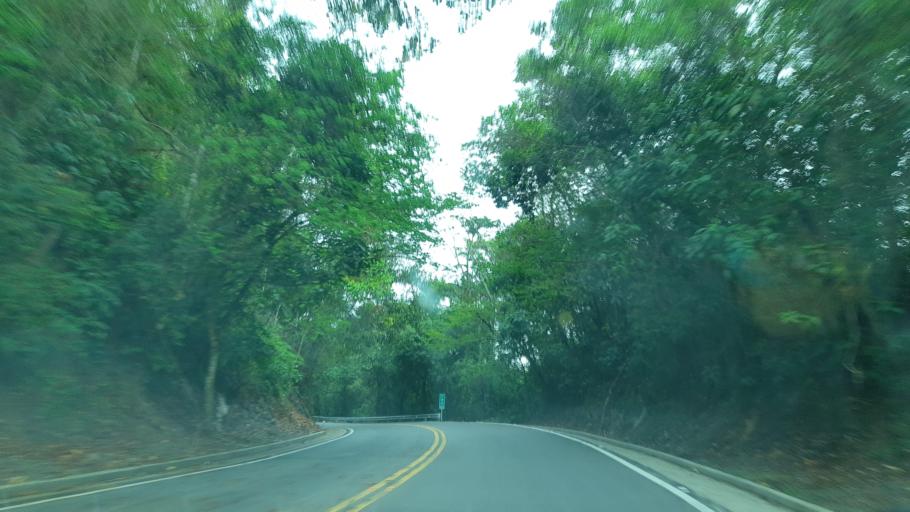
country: CO
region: Casanare
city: Sabanalarga
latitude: 4.7537
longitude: -73.0208
